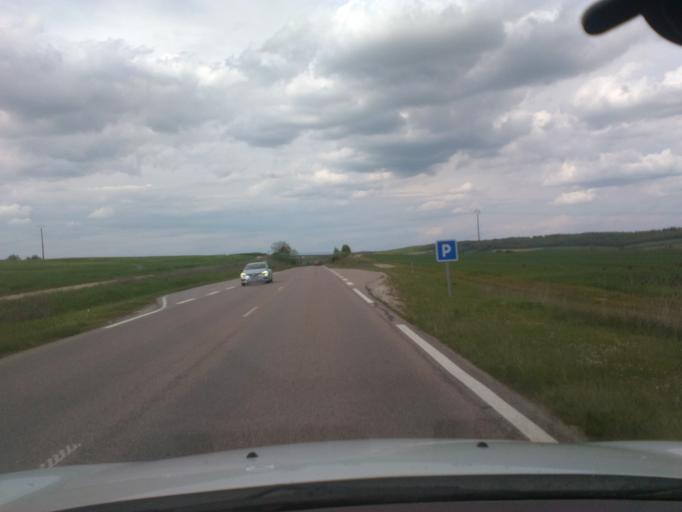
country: FR
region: Lorraine
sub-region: Departement des Vosges
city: Mirecourt
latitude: 48.2916
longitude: 6.1542
